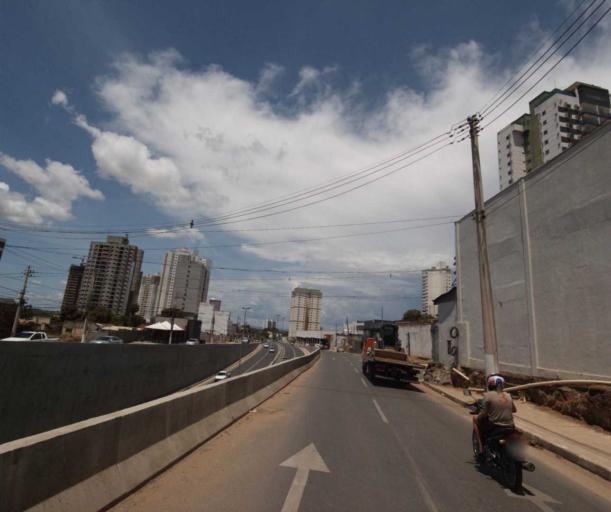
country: BR
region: Mato Grosso
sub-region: Cuiaba
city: Cuiaba
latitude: -15.5855
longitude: -56.1137
